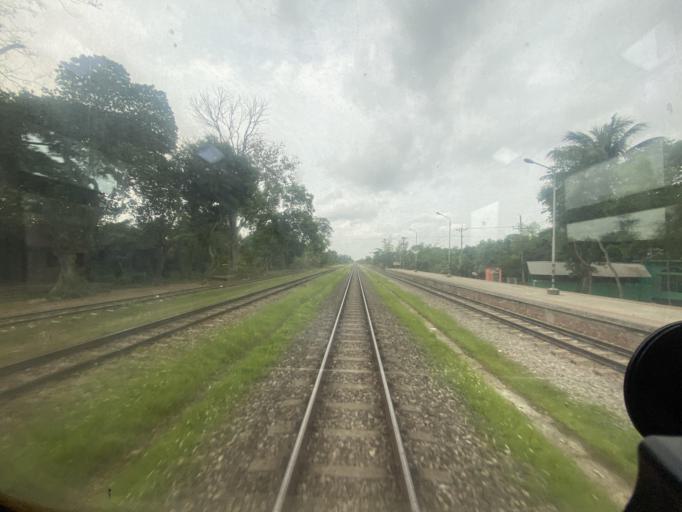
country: BD
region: Chittagong
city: Laksham
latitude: 23.2012
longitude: 91.1589
